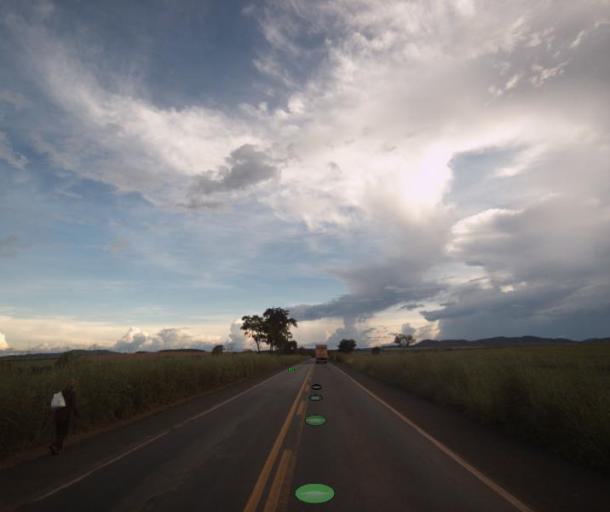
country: BR
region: Goias
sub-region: Uruacu
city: Uruacu
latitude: -14.1198
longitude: -49.1071
